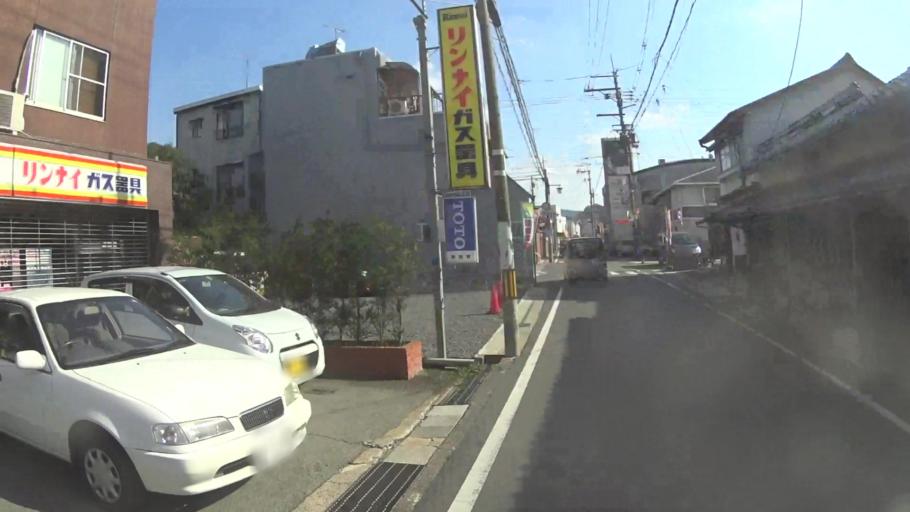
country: JP
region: Kyoto
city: Kameoka
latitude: 35.0089
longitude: 135.5835
